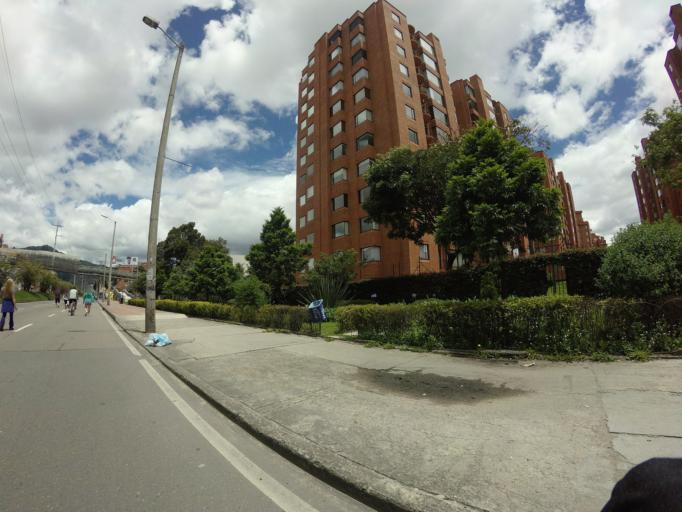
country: CO
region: Bogota D.C.
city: Barrio San Luis
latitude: 4.7089
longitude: -74.0328
